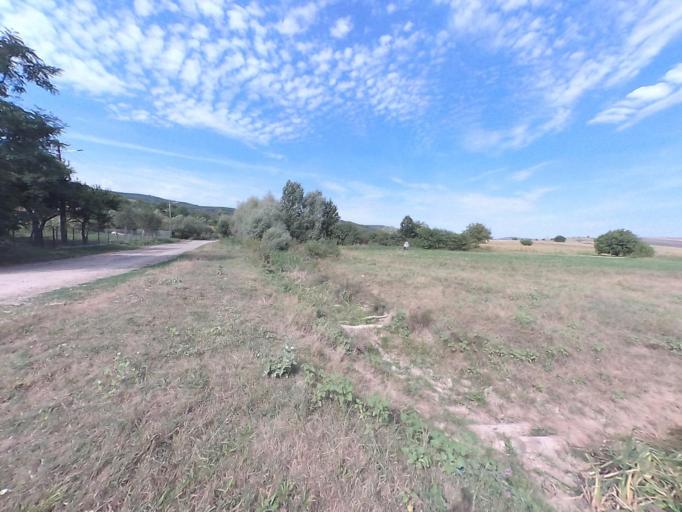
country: RO
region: Vaslui
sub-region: Comuna Osesti
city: Buda
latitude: 46.7623
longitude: 27.4183
